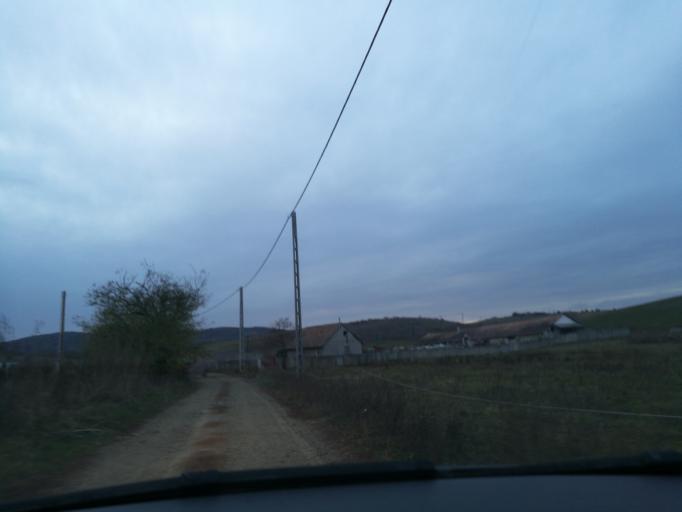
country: HU
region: Nograd
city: Bujak
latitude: 47.8659
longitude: 19.5616
